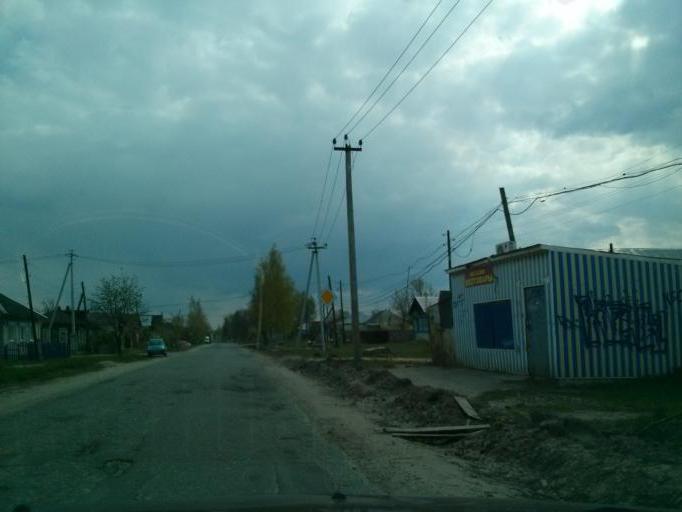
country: RU
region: Nizjnij Novgorod
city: Shimorskoye
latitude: 55.3384
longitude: 41.9286
